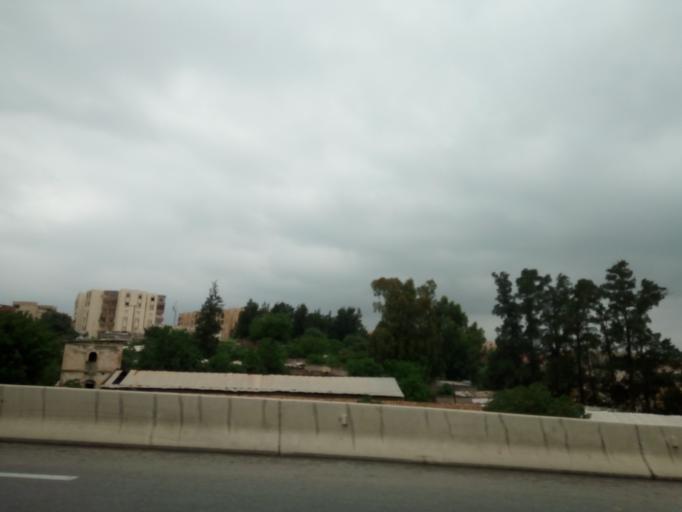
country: DZ
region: Blida
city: Chiffa
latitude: 36.4419
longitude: 2.7513
